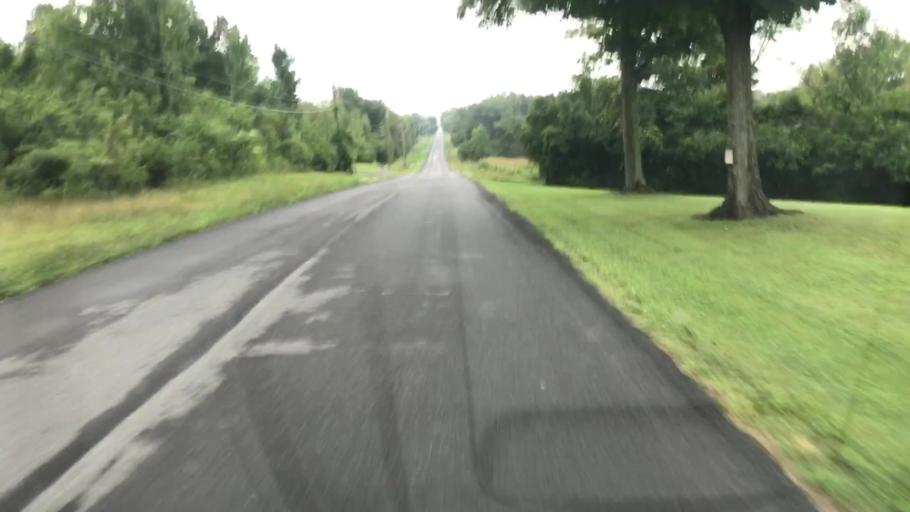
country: US
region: New York
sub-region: Onondaga County
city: Skaneateles
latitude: 42.9515
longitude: -76.4591
